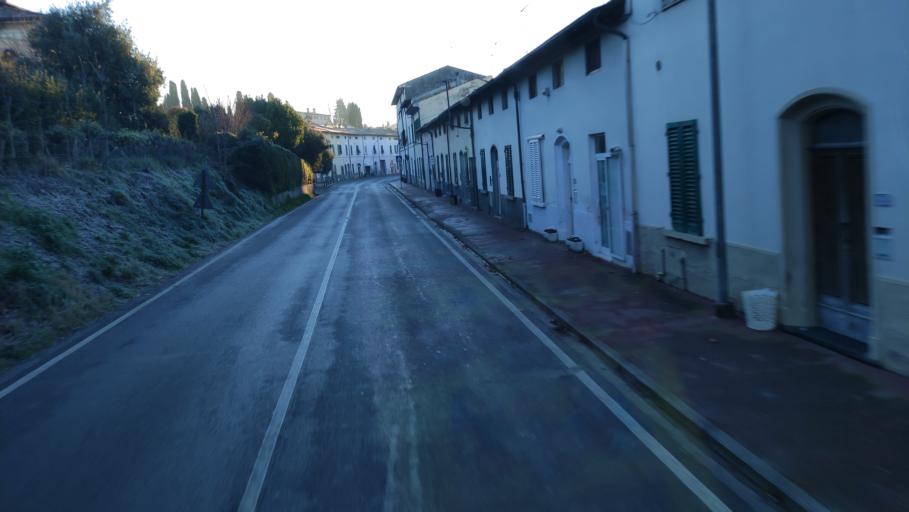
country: IT
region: Tuscany
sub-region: Province of Florence
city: Pozzale-Case Nuove
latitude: 43.6573
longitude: 10.9385
